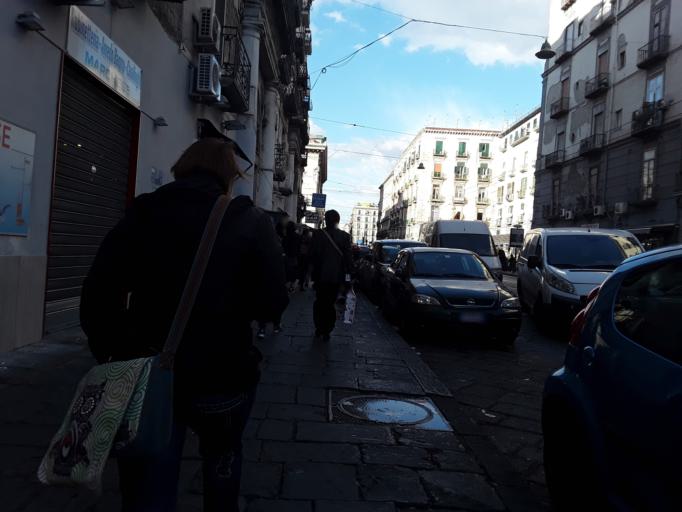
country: IT
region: Campania
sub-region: Provincia di Napoli
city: Napoli
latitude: 40.8495
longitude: 14.2685
